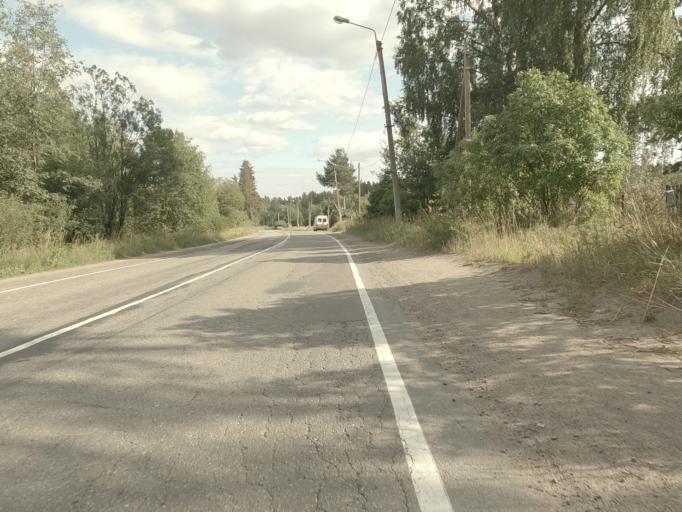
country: RU
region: Leningrad
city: Kamennogorsk
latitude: 60.9420
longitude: 29.1517
